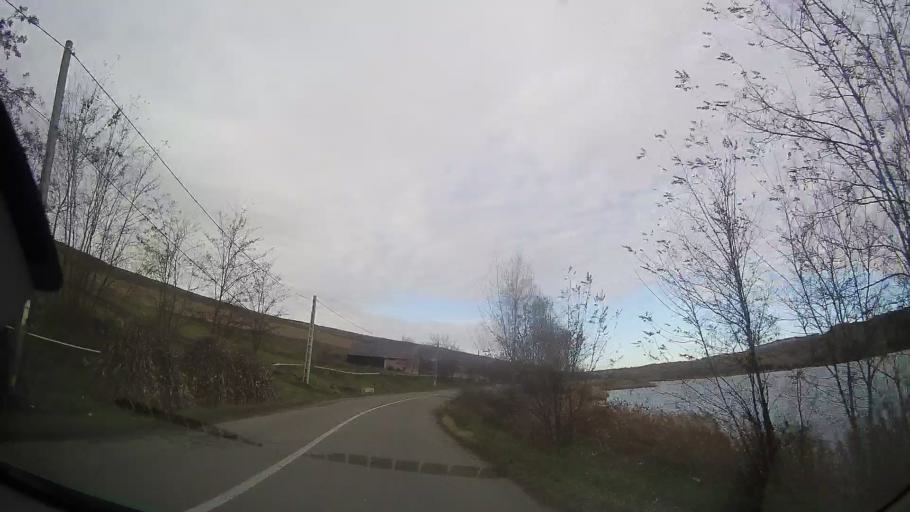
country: RO
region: Cluj
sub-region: Comuna Geaca
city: Geaca
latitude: 46.8396
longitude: 24.1281
